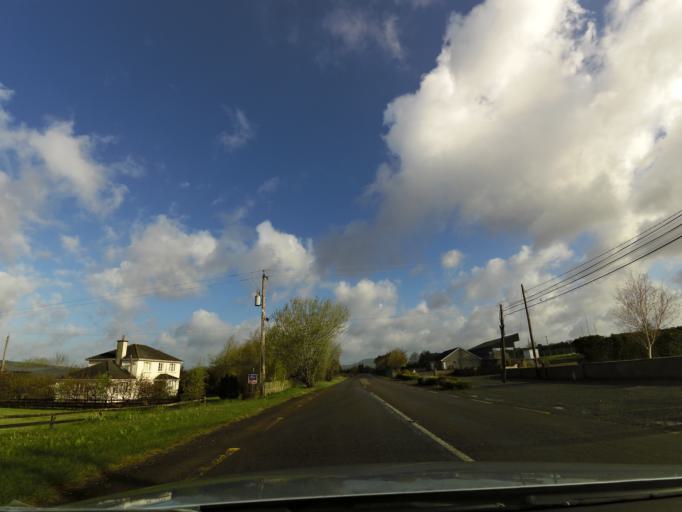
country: IE
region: Munster
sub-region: North Tipperary
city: Templemore
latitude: 52.7300
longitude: -7.9175
